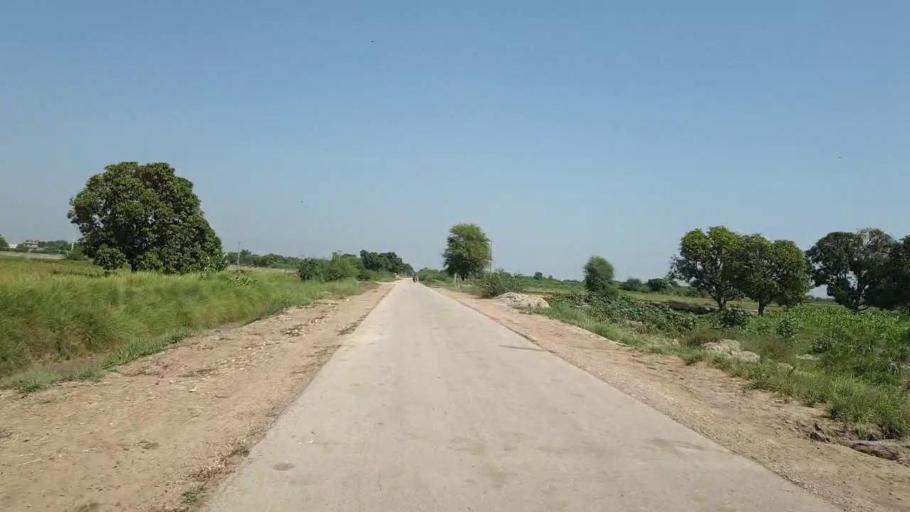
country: PK
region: Sindh
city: Hyderabad
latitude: 25.4605
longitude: 68.4249
